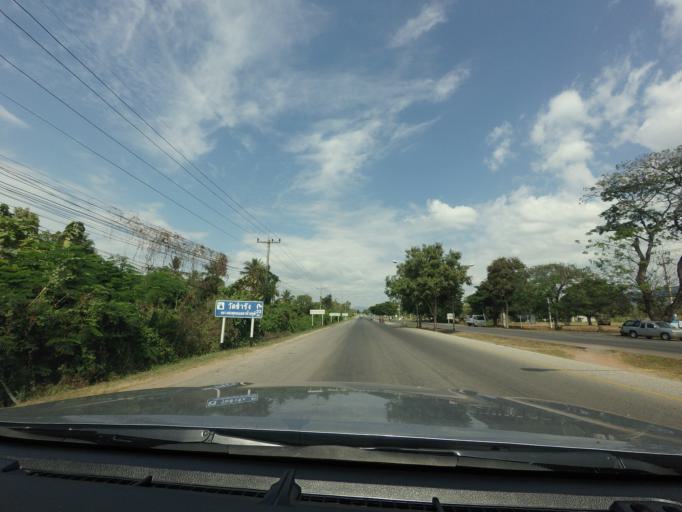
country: TH
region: Phitsanulok
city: Wang Thong
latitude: 16.7409
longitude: 100.4317
